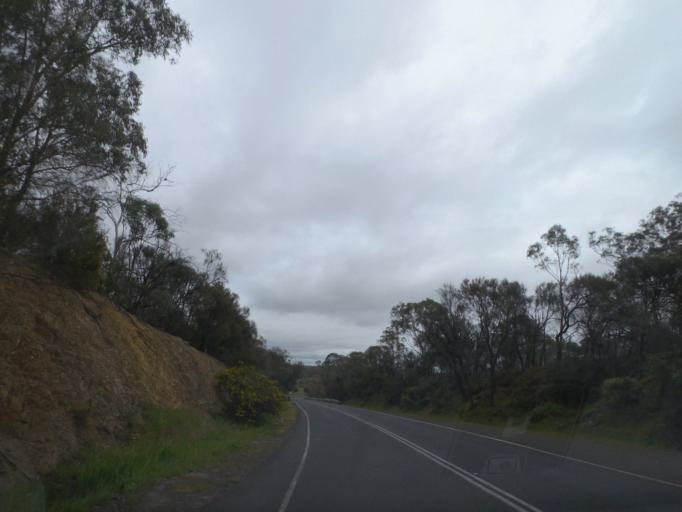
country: AU
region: Victoria
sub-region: Nillumbik
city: Doreen
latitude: -37.5701
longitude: 145.1259
